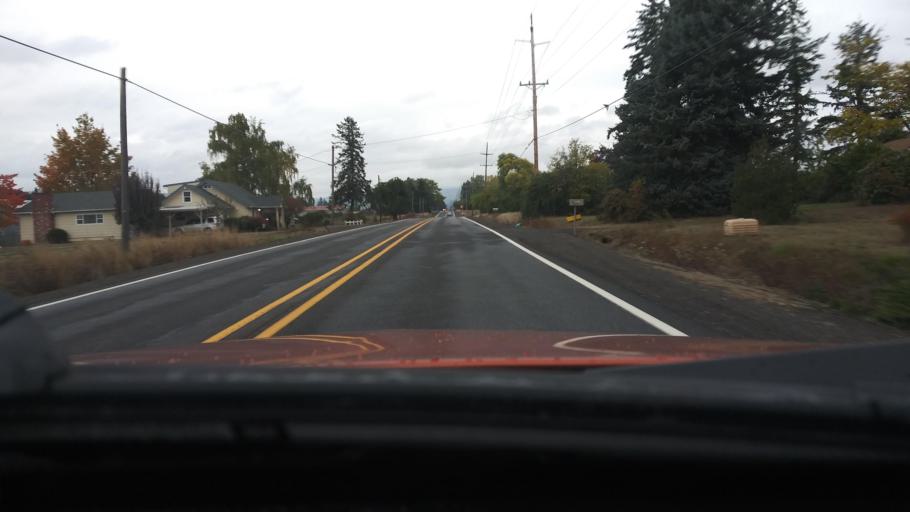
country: US
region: Oregon
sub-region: Washington County
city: Banks
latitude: 45.5976
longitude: -123.1145
